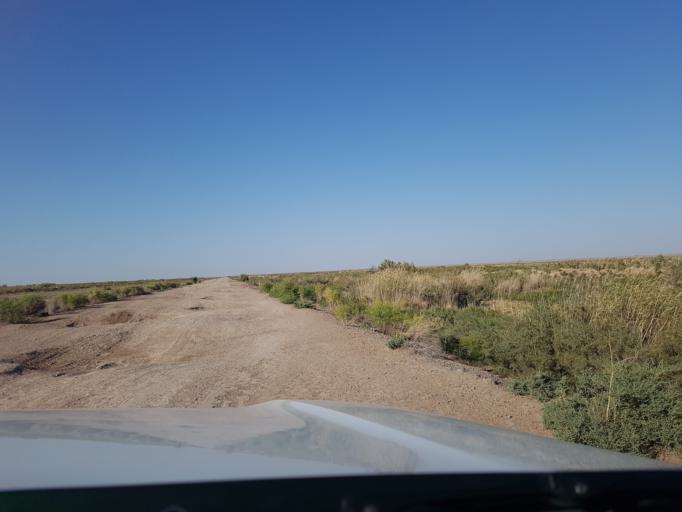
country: IR
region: Razavi Khorasan
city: Sarakhs
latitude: 36.9643
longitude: 61.3829
